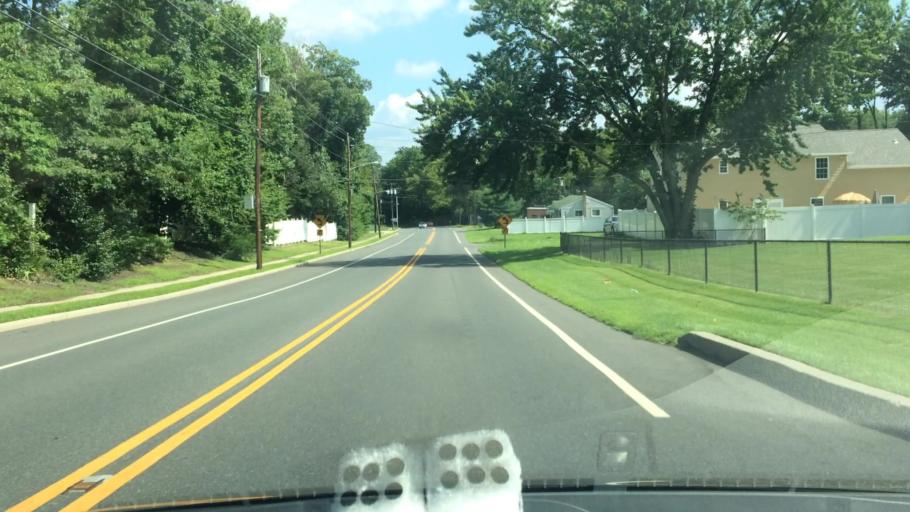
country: US
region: New Jersey
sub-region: Camden County
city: Blackwood
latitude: 39.7971
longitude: -75.0867
